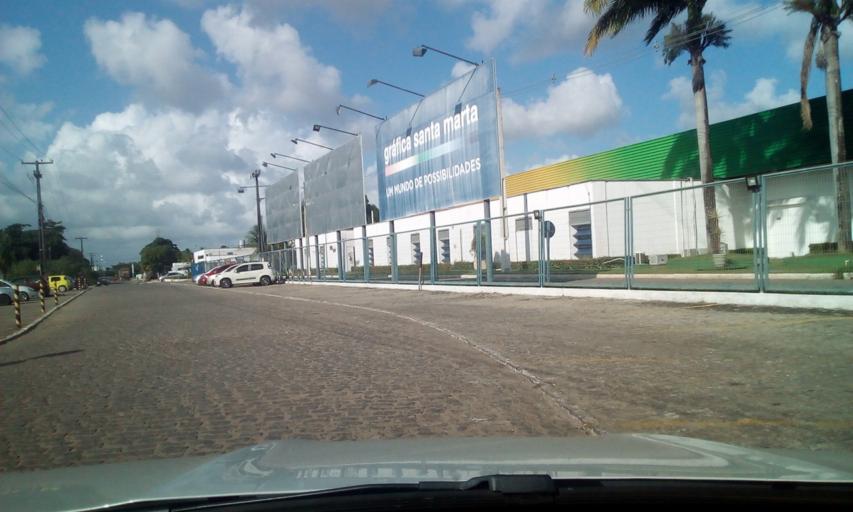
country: BR
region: Paraiba
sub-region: Conde
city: Conde
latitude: -7.1967
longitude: -34.9054
